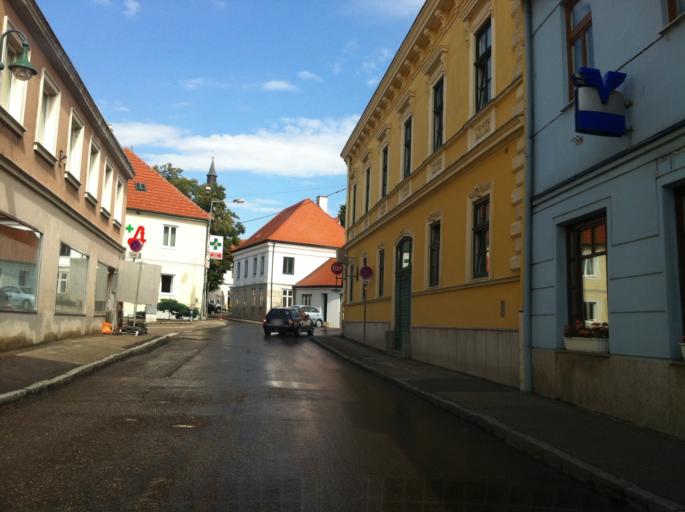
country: AT
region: Lower Austria
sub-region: Politischer Bezirk Tulln
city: Sieghartskirchen
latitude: 48.2546
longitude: 16.0135
